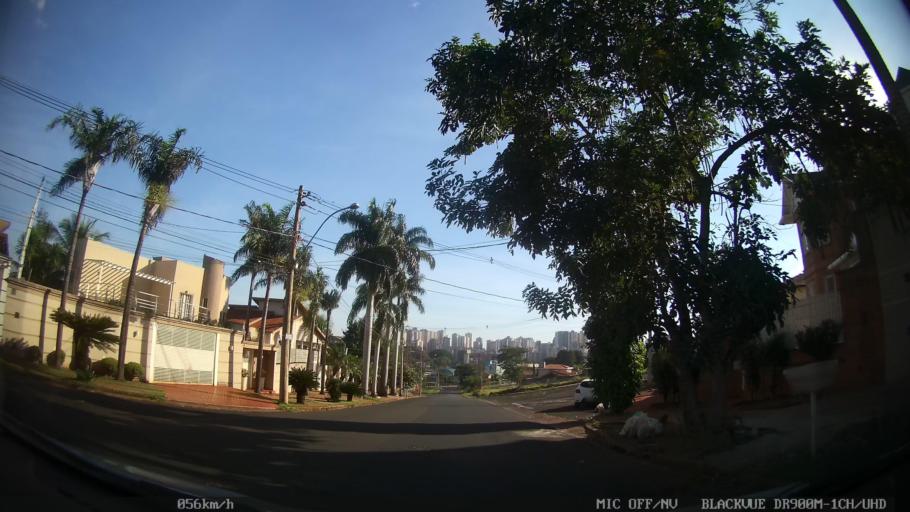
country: BR
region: Sao Paulo
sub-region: Ribeirao Preto
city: Ribeirao Preto
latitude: -21.2069
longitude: -47.7821
